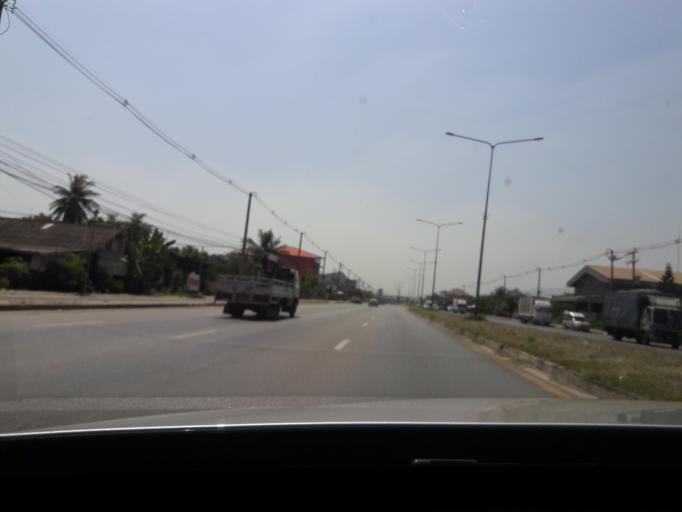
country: TH
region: Bangkok
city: Nong Khaem
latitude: 13.6657
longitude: 100.3152
